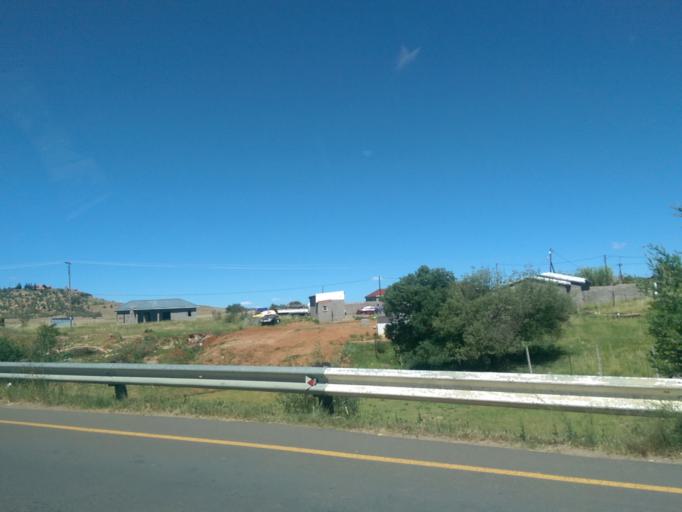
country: LS
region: Maseru
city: Maseru
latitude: -29.3873
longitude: 27.5600
